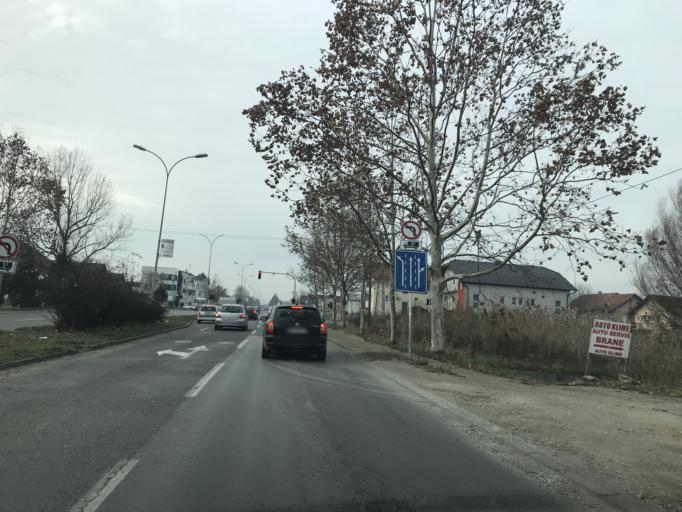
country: RS
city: Veternik
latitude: 45.2466
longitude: 19.7689
